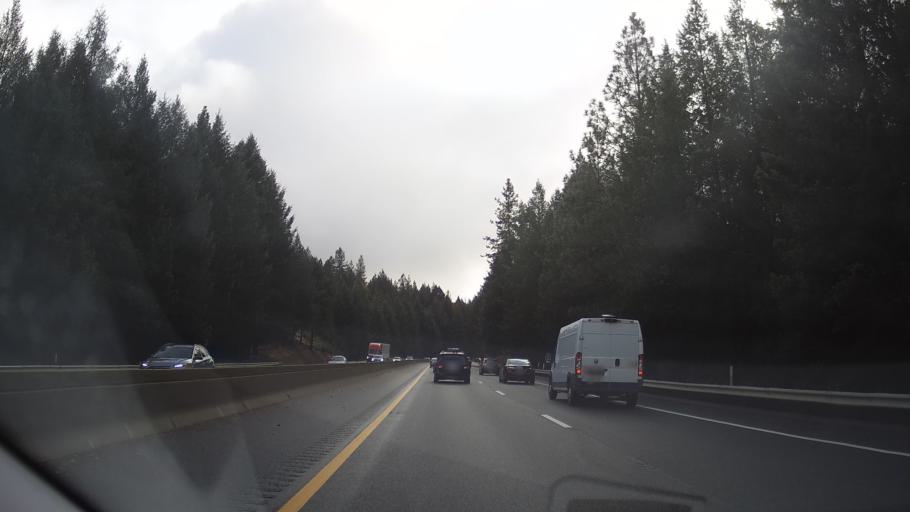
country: US
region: California
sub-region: Placer County
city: Colfax
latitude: 39.0694
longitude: -120.9645
